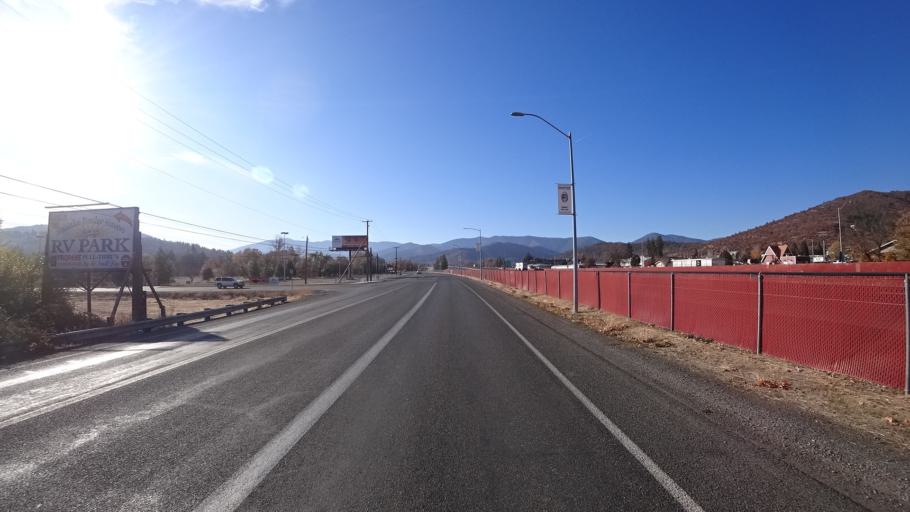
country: US
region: California
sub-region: Siskiyou County
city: Yreka
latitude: 41.7098
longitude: -122.6416
